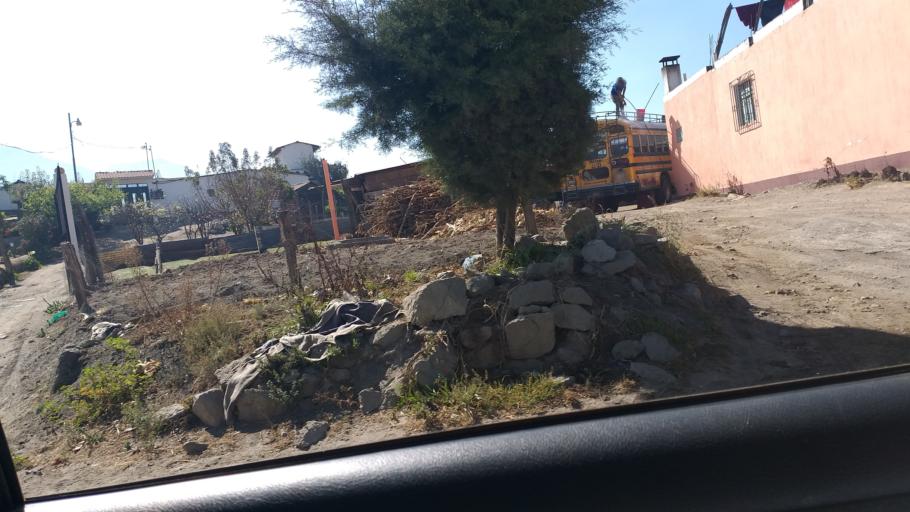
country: GT
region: Quetzaltenango
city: Quetzaltenango
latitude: 14.7996
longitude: -91.5467
